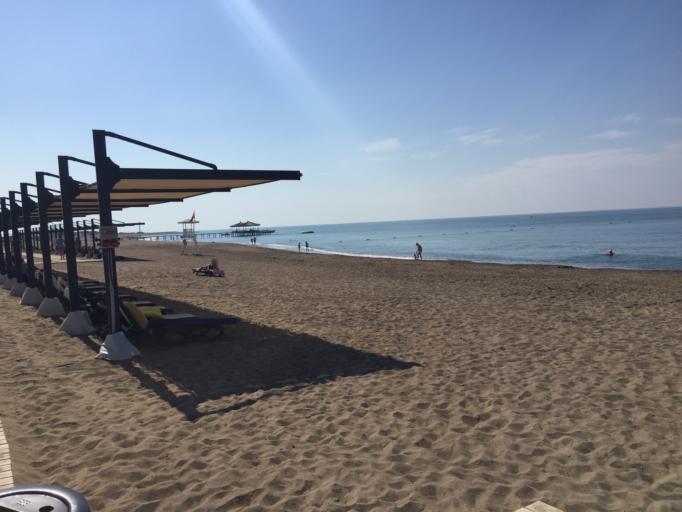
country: TR
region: Antalya
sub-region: Serik
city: Bogazkent
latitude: 36.8373
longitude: 31.1179
